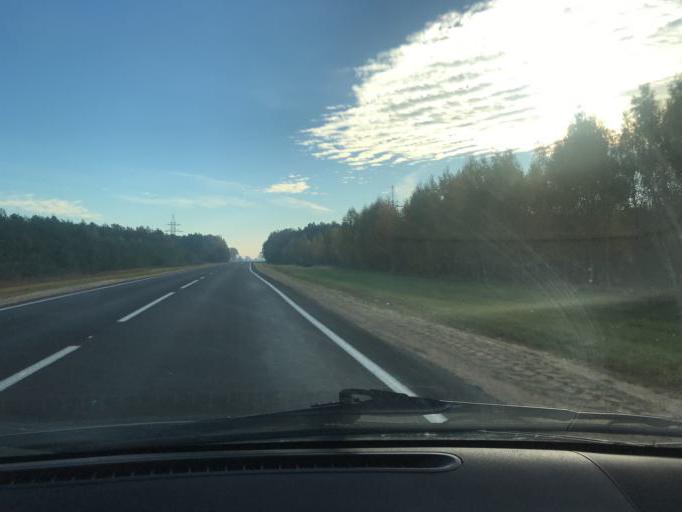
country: BY
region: Brest
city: Drahichyn
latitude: 52.2247
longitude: 25.1444
